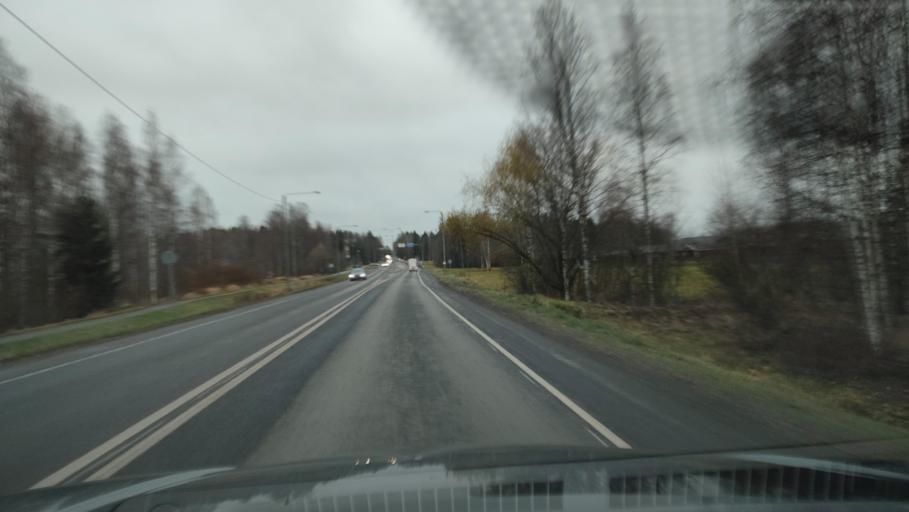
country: FI
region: Southern Ostrobothnia
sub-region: Seinaejoki
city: Ilmajoki
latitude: 62.7727
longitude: 22.6836
